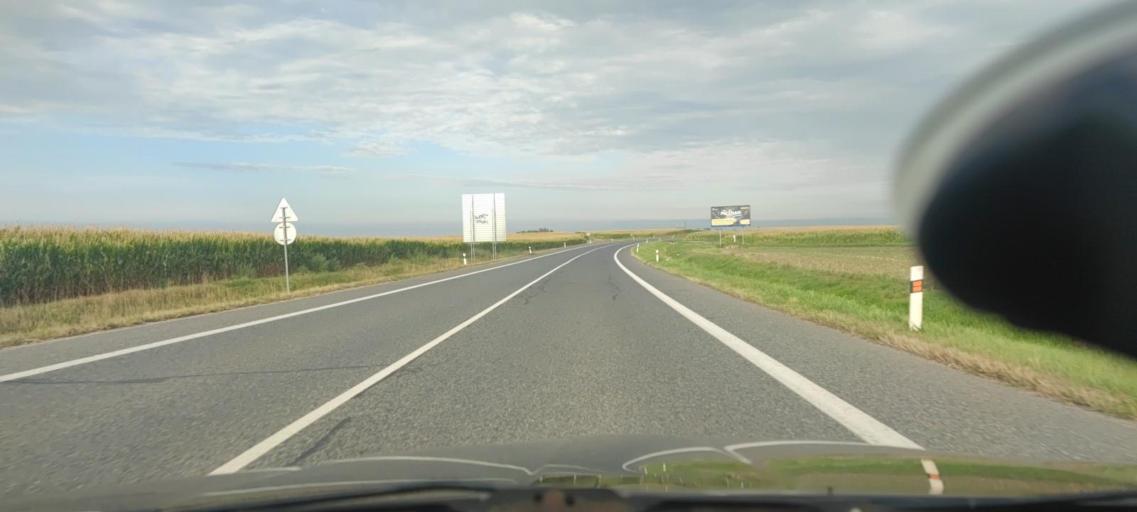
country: CZ
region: South Moravian
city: Pohorelice
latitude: 48.9700
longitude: 16.5133
